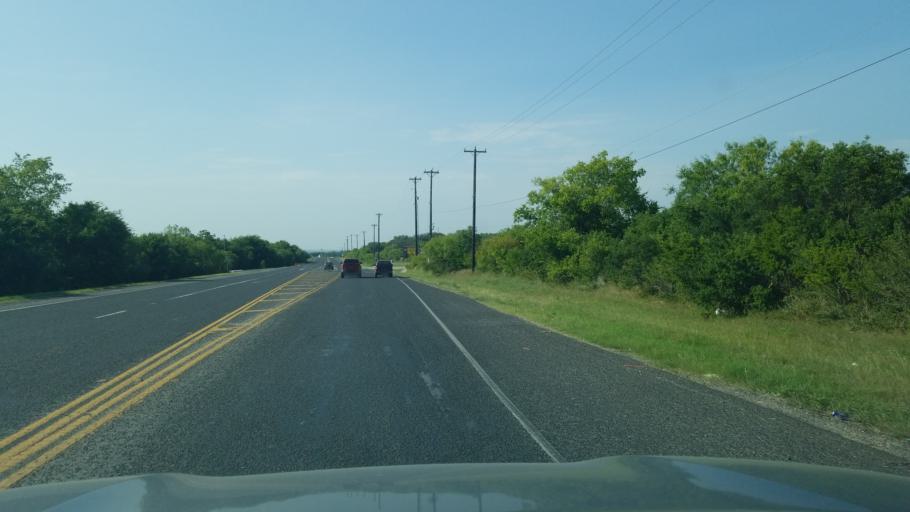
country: US
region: Texas
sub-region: Medina County
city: La Coste
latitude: 29.4132
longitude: -98.7811
